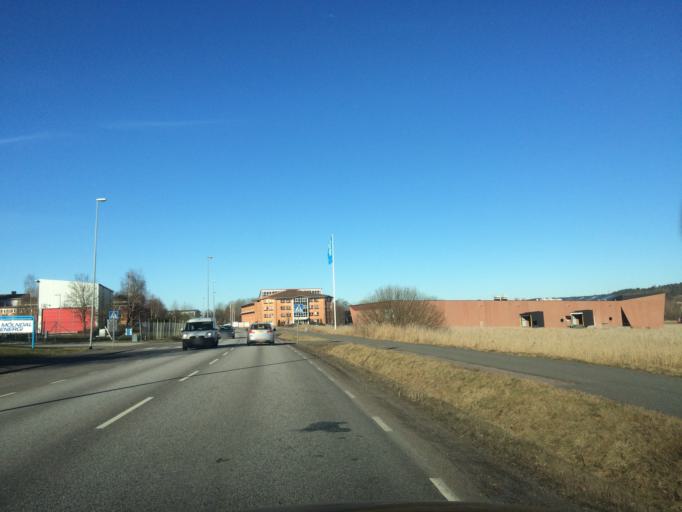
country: SE
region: Vaestra Goetaland
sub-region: Molndal
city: Moelndal
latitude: 57.6413
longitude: 11.9989
